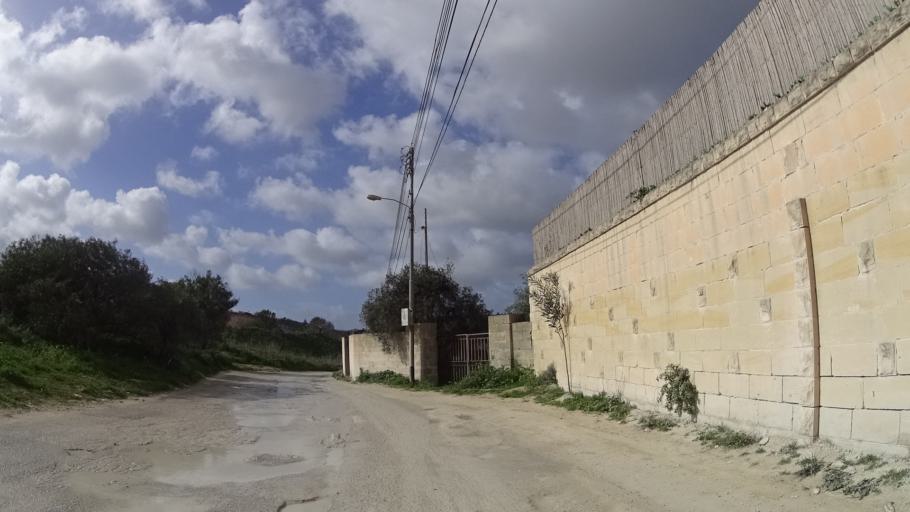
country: MT
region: In-Naxxar
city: Naxxar
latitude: 35.9260
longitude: 14.4363
